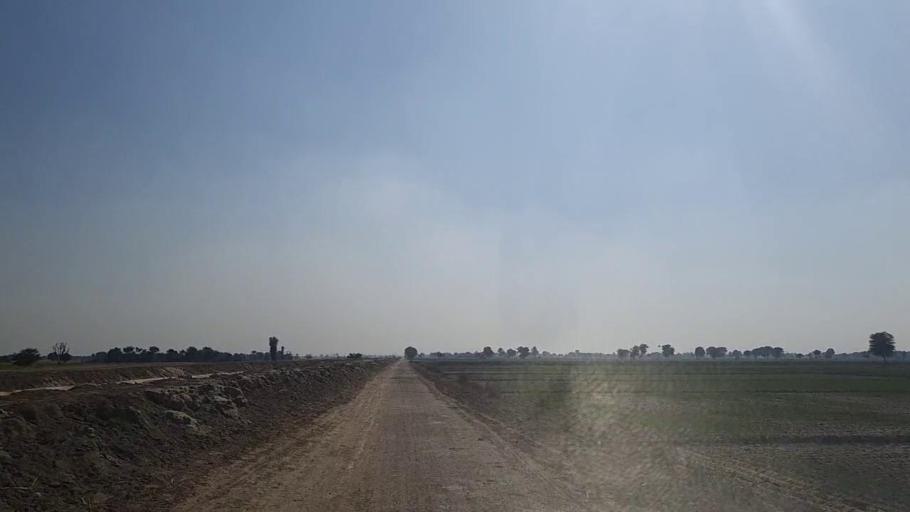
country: PK
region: Sindh
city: Shahpur Chakar
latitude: 26.2165
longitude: 68.5840
